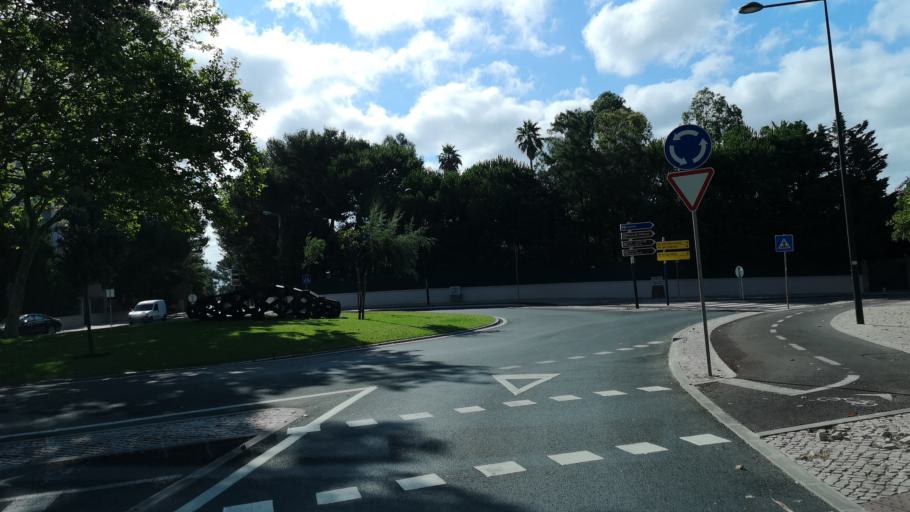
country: PT
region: Lisbon
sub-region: Cascais
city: Cascais
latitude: 38.6945
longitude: -9.4310
